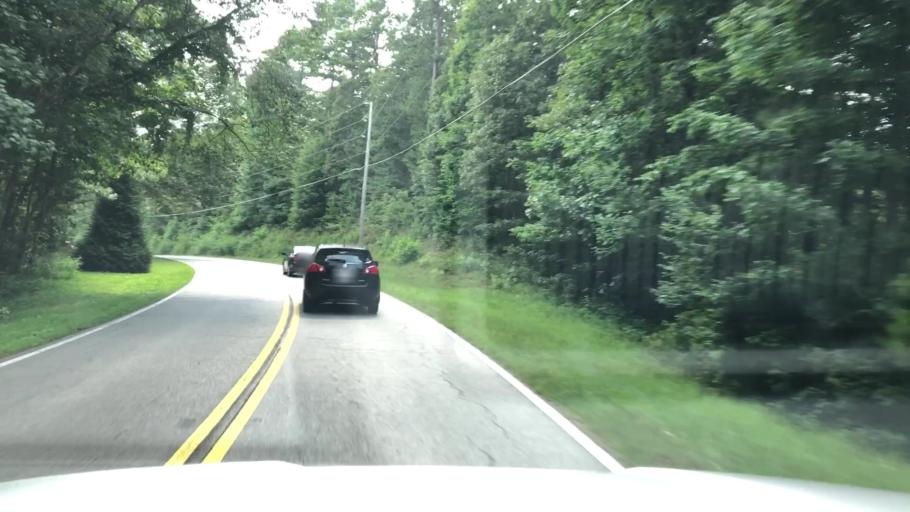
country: US
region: Georgia
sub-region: Paulding County
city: Dallas
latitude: 33.9747
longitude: -84.8202
